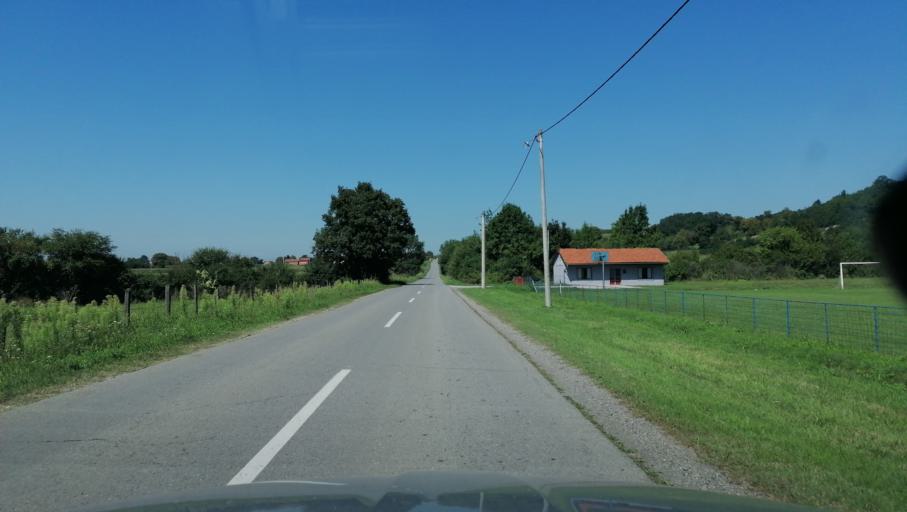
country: RS
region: Central Serbia
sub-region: Raski Okrug
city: Vrnjacka Banja
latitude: 43.6841
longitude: 20.8850
